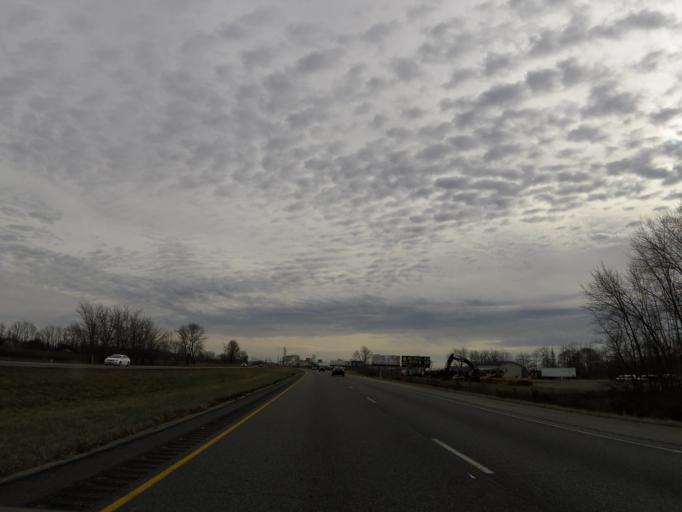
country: US
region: Indiana
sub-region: Hendricks County
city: Pittsboro
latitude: 39.8803
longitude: -86.5048
